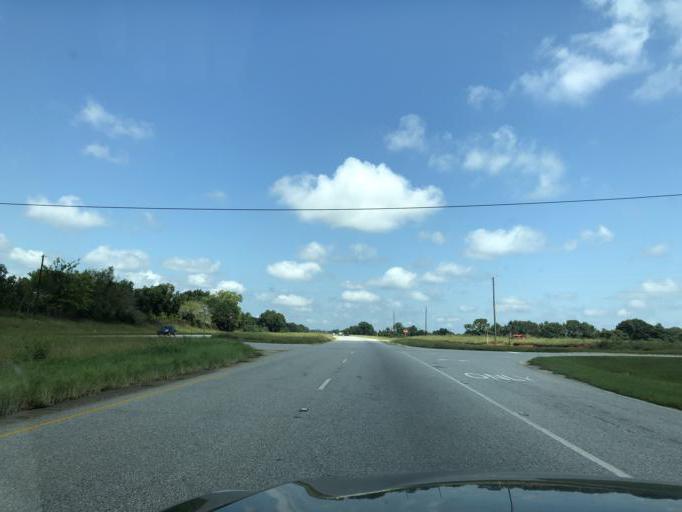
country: US
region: Alabama
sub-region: Henry County
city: Abbeville
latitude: 31.5950
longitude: -85.2772
